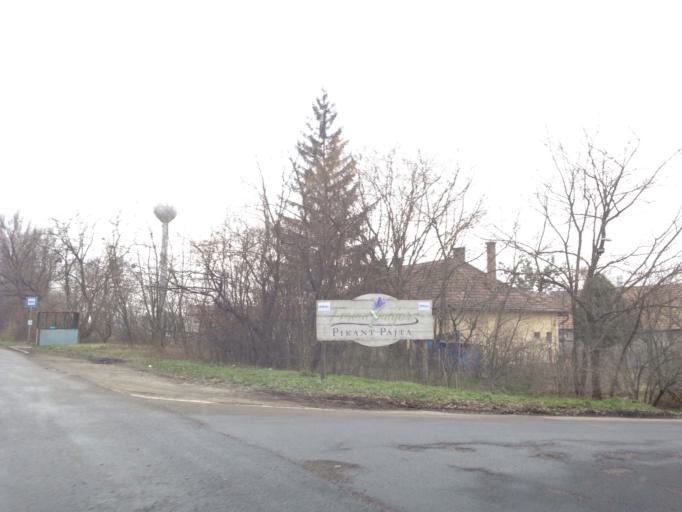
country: HU
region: Komarom-Esztergom
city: Szomod
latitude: 47.6937
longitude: 18.3082
